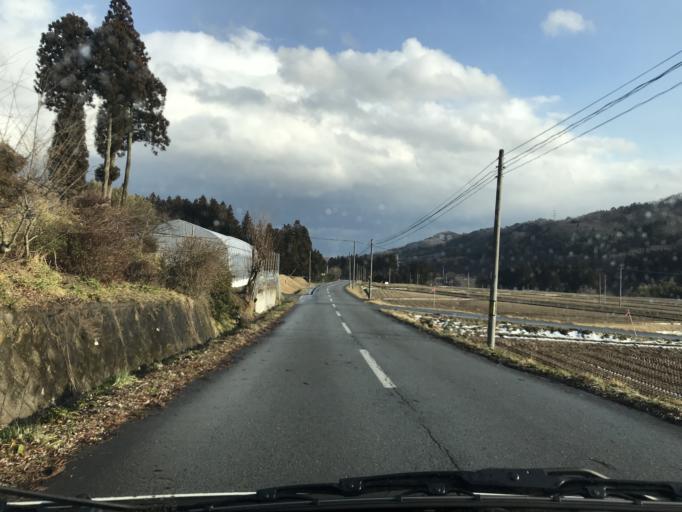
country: JP
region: Iwate
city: Mizusawa
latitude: 39.0816
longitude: 141.0015
